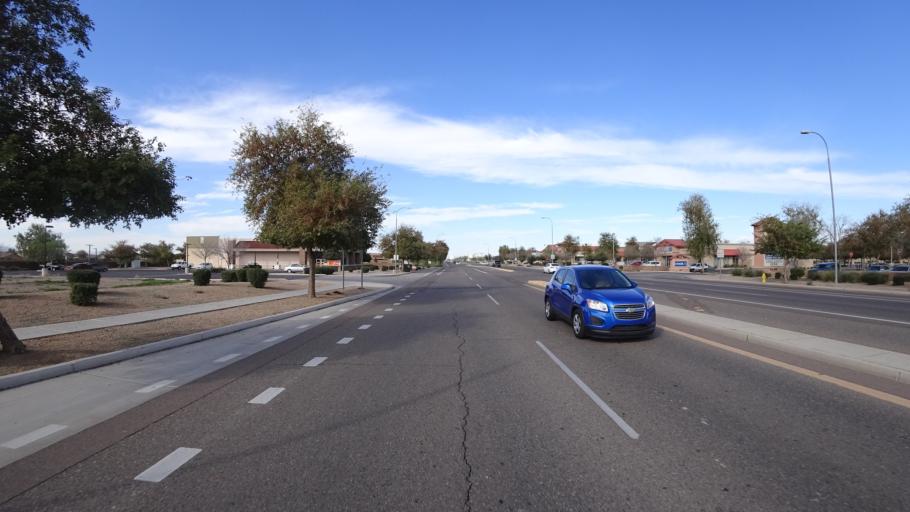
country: US
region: Arizona
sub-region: Maricopa County
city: Tolleson
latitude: 33.4227
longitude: -112.2727
